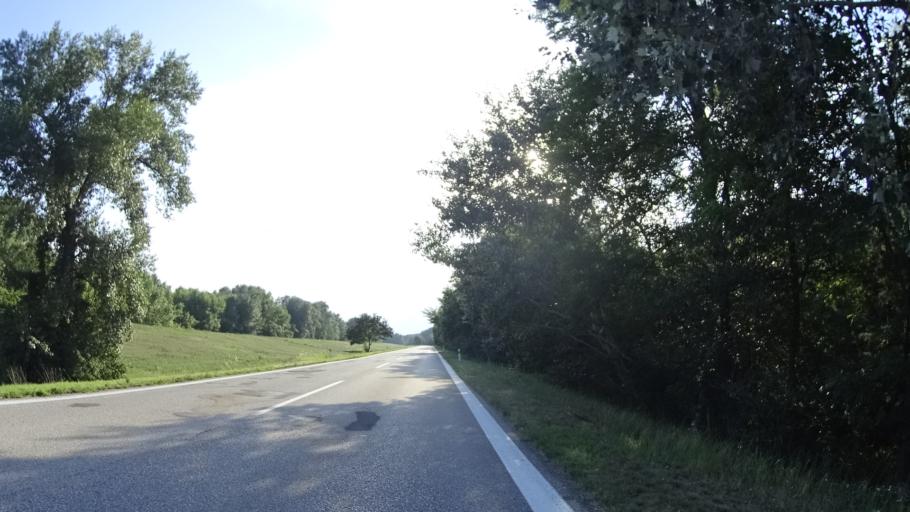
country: HU
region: Komarom-Esztergom
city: Nyergesujfalu
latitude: 47.7738
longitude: 18.5557
